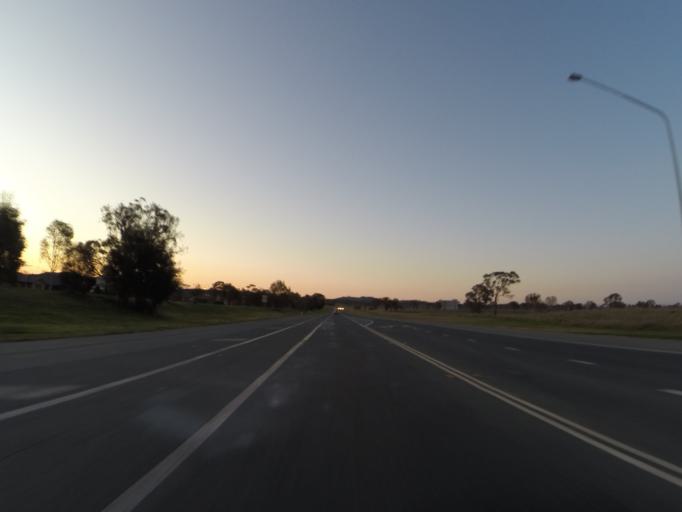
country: AU
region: Australian Capital Territory
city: Kaleen
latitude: -35.1943
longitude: 149.1616
